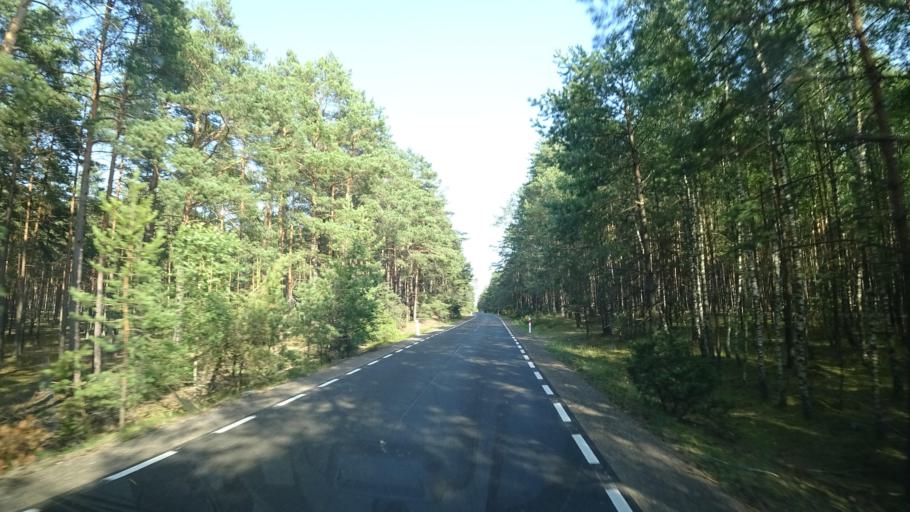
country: PL
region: Pomeranian Voivodeship
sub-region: Powiat chojnicki
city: Chojnice
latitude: 53.8605
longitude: 17.5284
